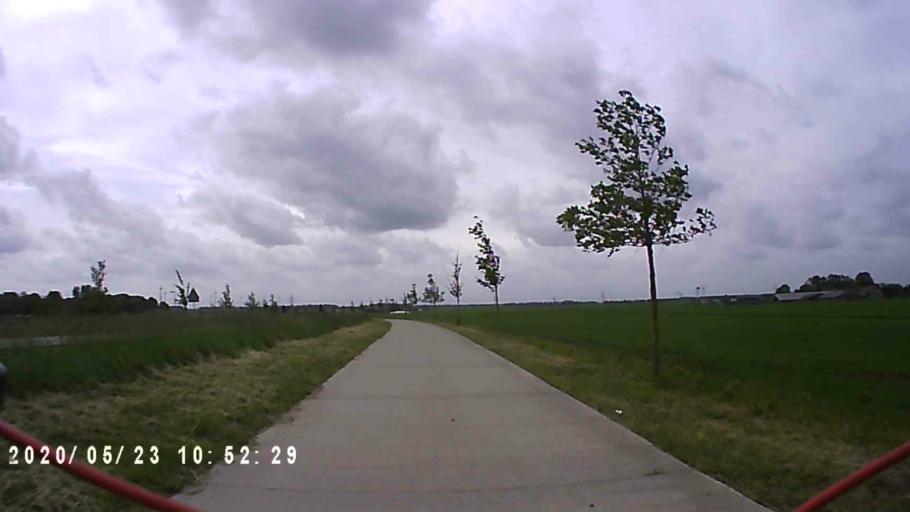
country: NL
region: Groningen
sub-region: Gemeente Delfzijl
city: Delfzijl
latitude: 53.3126
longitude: 6.9414
